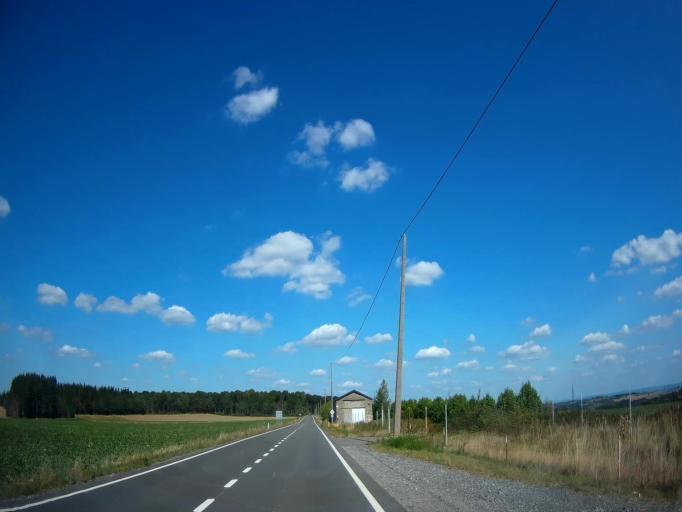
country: FR
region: Champagne-Ardenne
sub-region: Departement des Ardennes
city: Fromelennes
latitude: 50.1728
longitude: 4.9044
